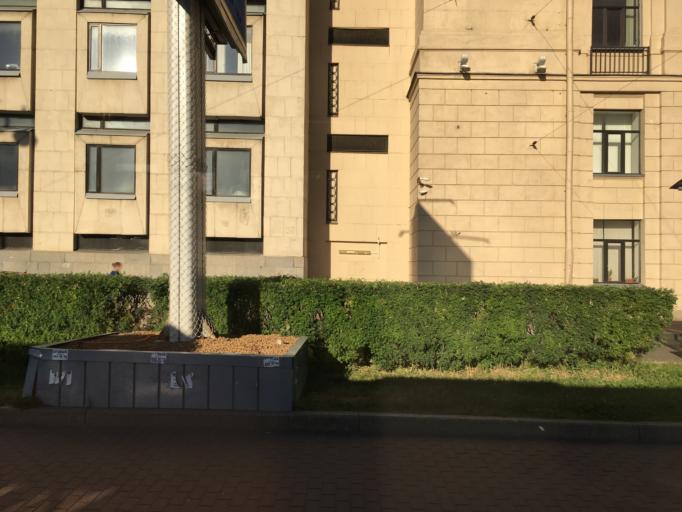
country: RU
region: St.-Petersburg
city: Admiralteisky
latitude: 59.8805
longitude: 30.3203
